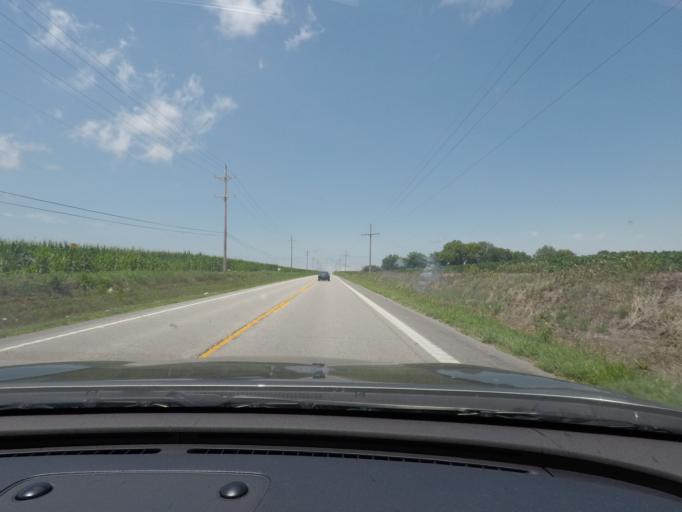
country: US
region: Missouri
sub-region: Saline County
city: Marshall
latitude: 39.1714
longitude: -93.2922
